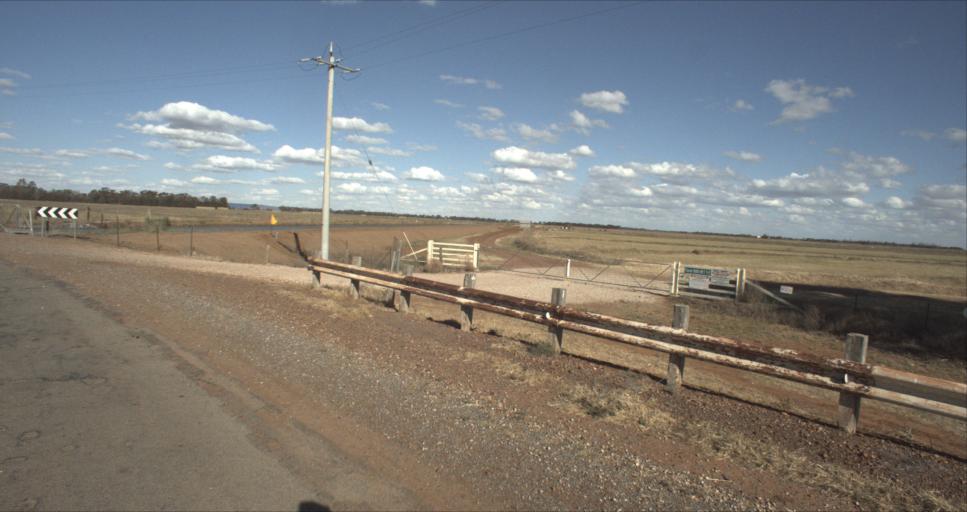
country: AU
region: New South Wales
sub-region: Leeton
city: Leeton
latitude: -34.4583
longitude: 146.2698
